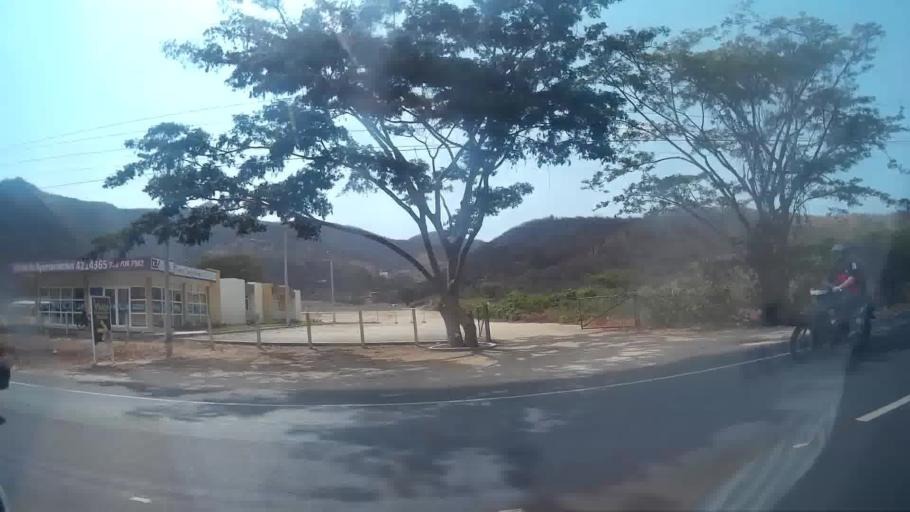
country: CO
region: Magdalena
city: Santa Marta
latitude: 11.2031
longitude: -74.1978
